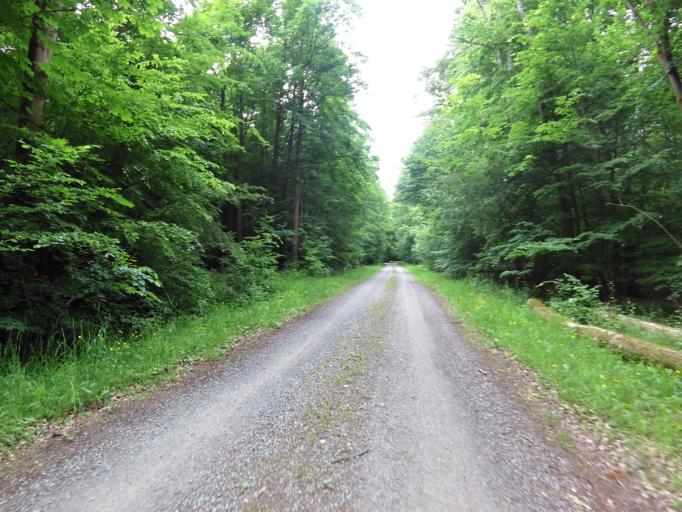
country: DE
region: Bavaria
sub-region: Regierungsbezirk Unterfranken
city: Wuerzburg
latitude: 49.7428
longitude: 9.8757
